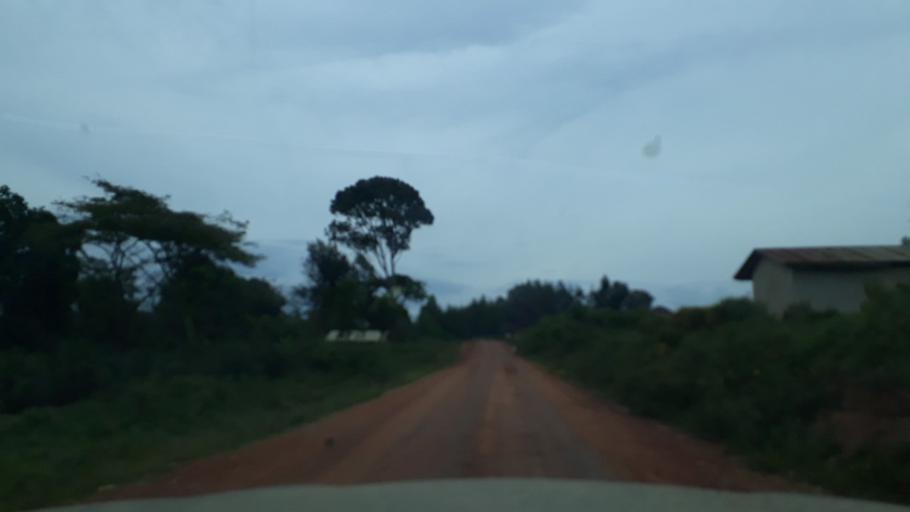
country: UG
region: Northern Region
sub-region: Zombo District
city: Paidha
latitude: 2.1930
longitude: 30.7279
